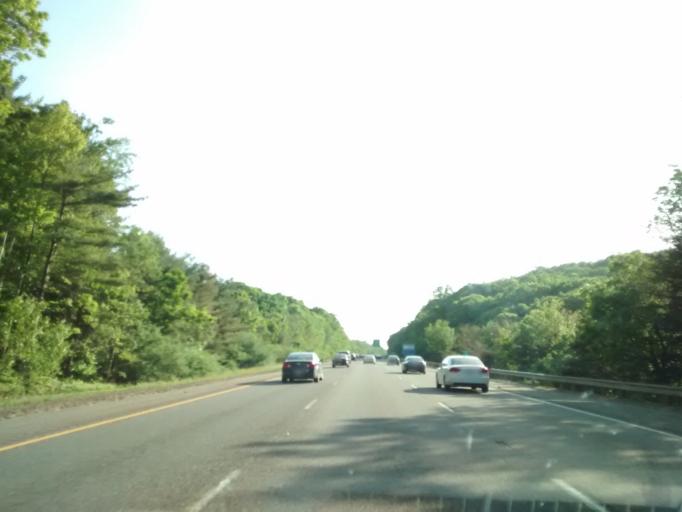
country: US
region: Massachusetts
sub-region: Worcester County
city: Shrewsbury
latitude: 42.3297
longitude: -71.6943
